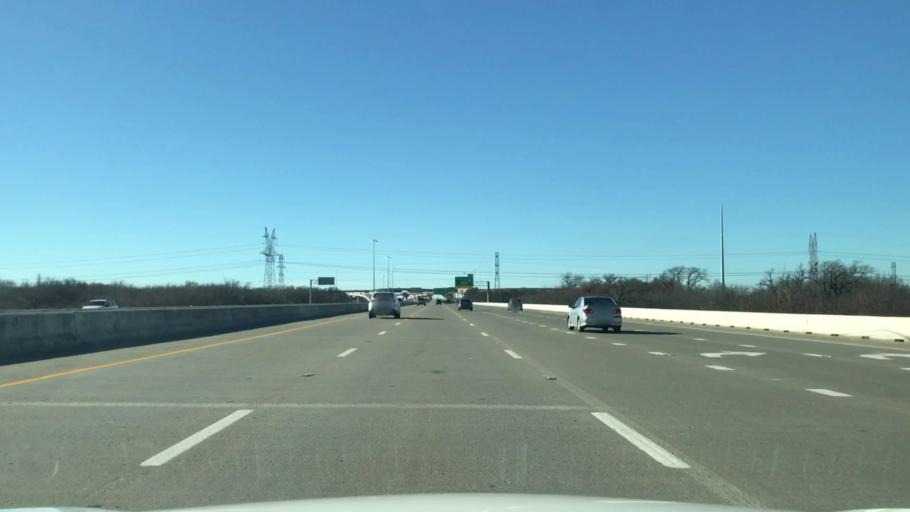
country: US
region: Texas
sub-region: Denton County
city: Lewisville
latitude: 33.0085
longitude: -96.9479
